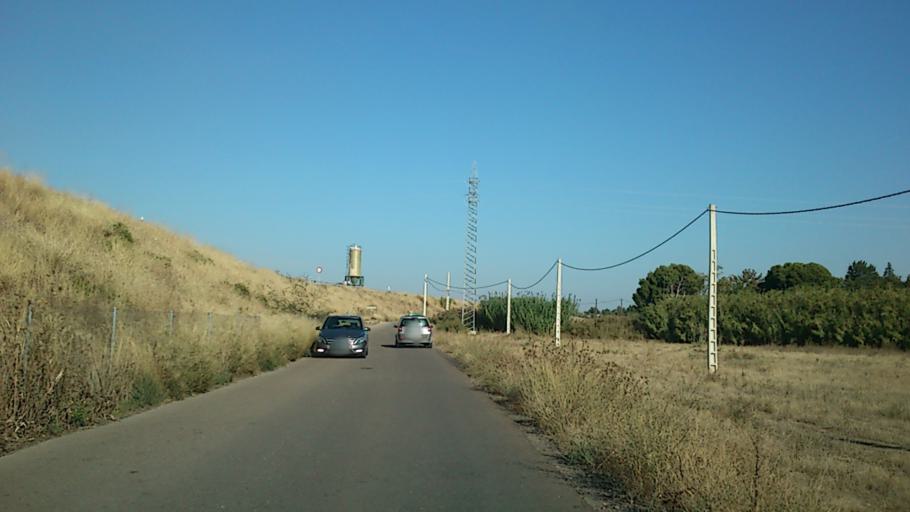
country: ES
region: Aragon
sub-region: Provincia de Zaragoza
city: Zaragoza
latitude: 41.6908
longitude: -0.8332
